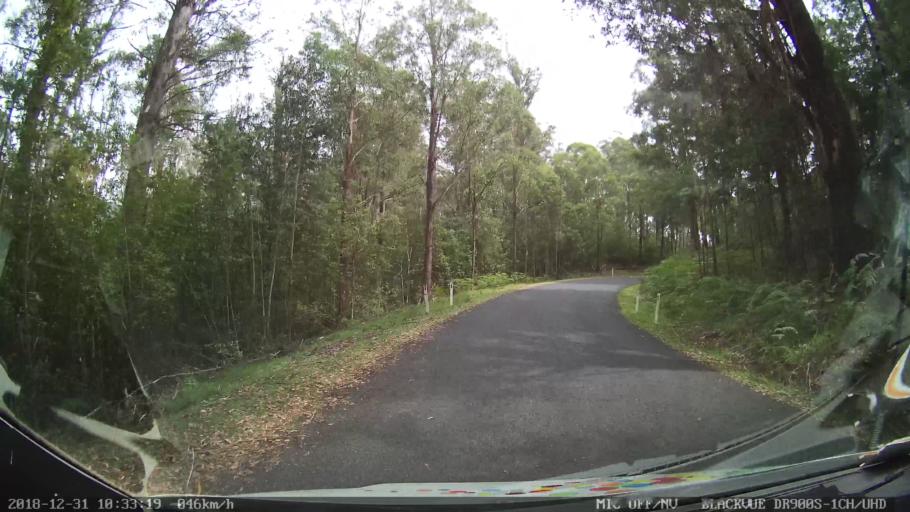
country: AU
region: New South Wales
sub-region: Snowy River
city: Jindabyne
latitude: -36.4475
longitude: 148.1639
